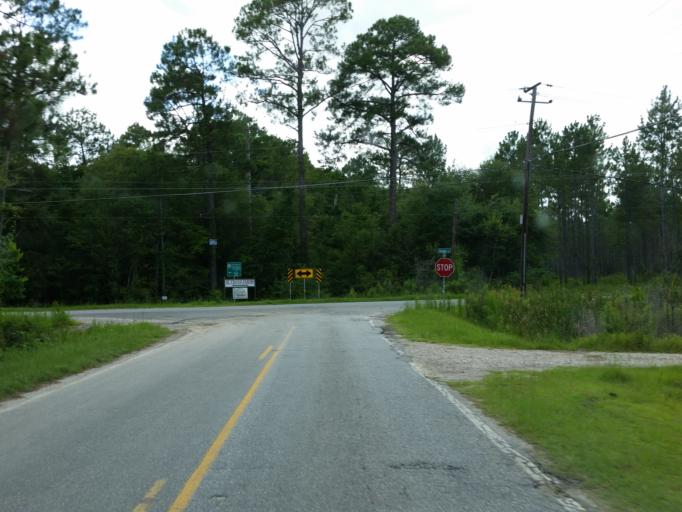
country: US
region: Georgia
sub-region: Tift County
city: Unionville
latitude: 31.3572
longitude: -83.5053
